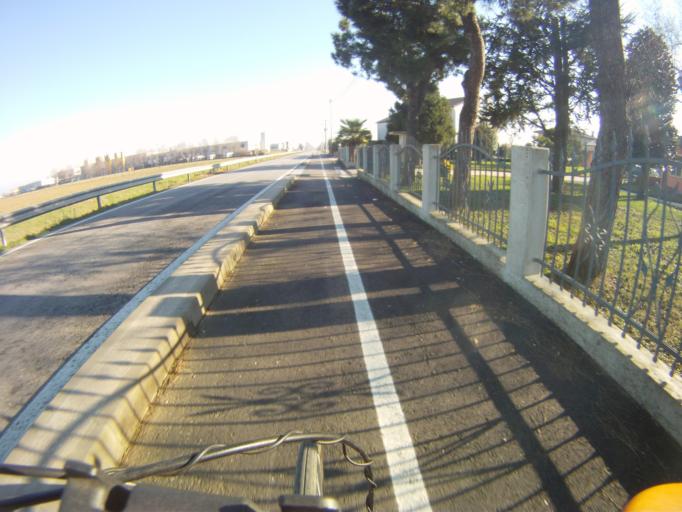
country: IT
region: Veneto
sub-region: Provincia di Padova
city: Brugine
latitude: 45.3092
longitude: 11.9887
